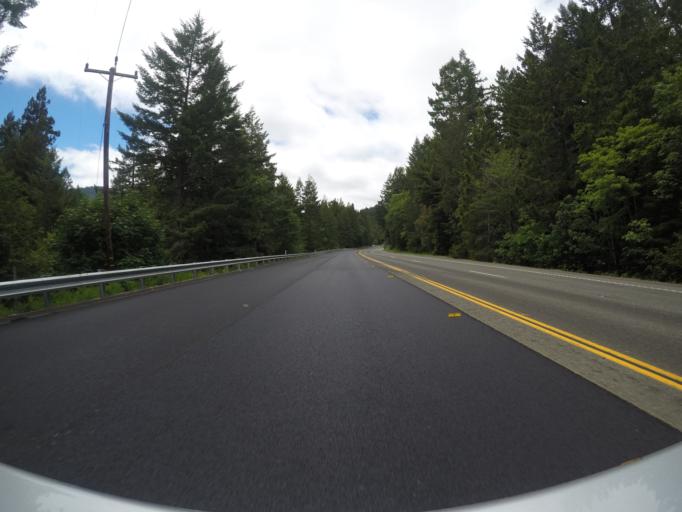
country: US
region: California
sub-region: Humboldt County
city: Redway
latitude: 40.3081
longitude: -123.9046
